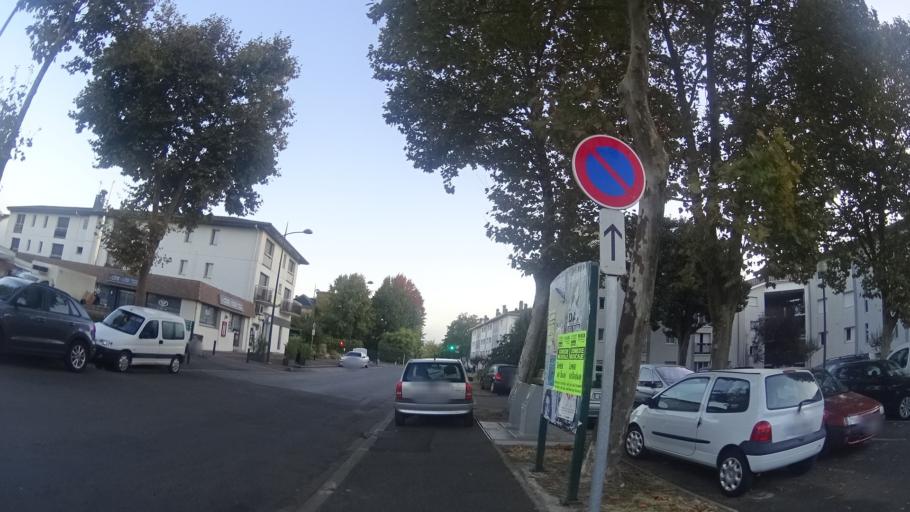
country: FR
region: Aquitaine
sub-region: Departement des Landes
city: Saint-Paul-les-Dax
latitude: 43.7235
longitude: -1.0533
